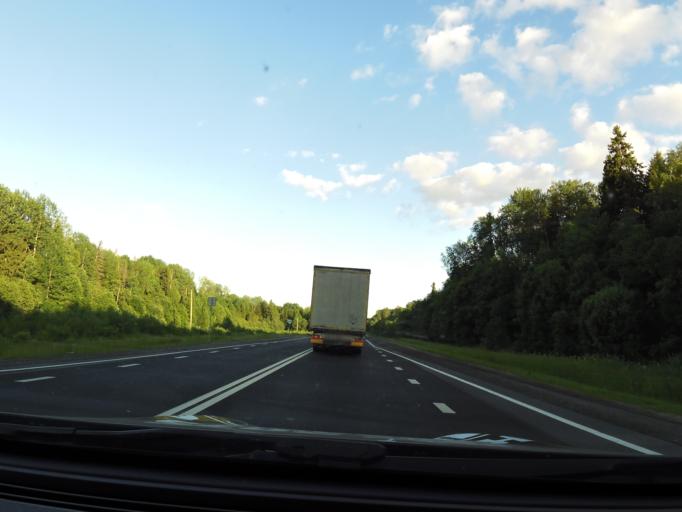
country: RU
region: Vologda
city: Gryazovets
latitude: 58.9753
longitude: 40.1498
